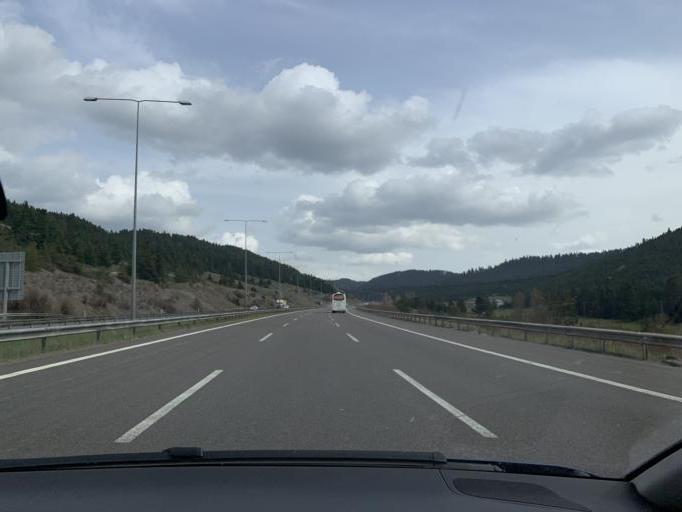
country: TR
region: Ankara
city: Pecenek
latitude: 40.6106
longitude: 32.2713
